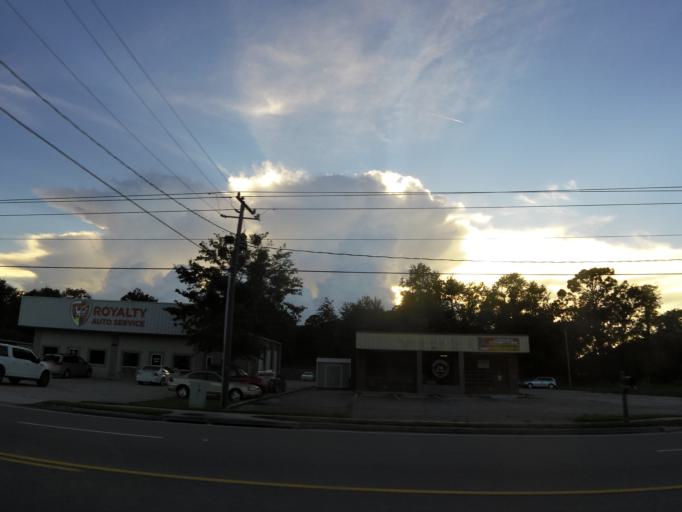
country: US
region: Georgia
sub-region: Camden County
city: St Marys
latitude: 30.7551
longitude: -81.5763
